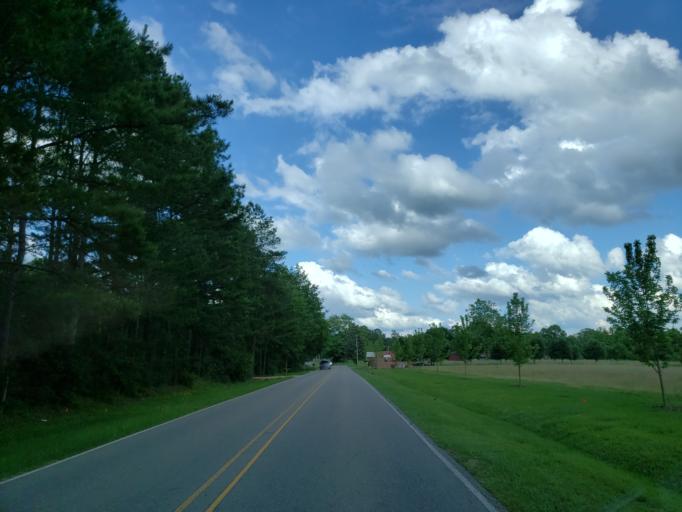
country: US
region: Mississippi
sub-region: Forrest County
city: Petal
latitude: 31.3104
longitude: -89.2185
